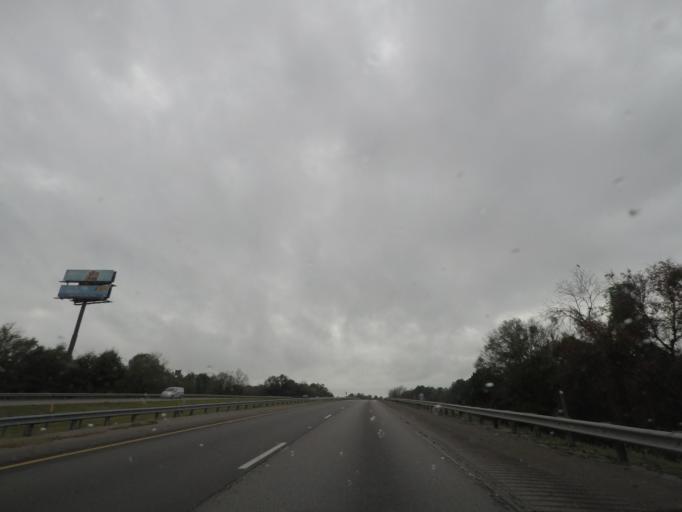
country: US
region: South Carolina
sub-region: Orangeburg County
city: Holly Hill
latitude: 33.5254
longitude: -80.4278
